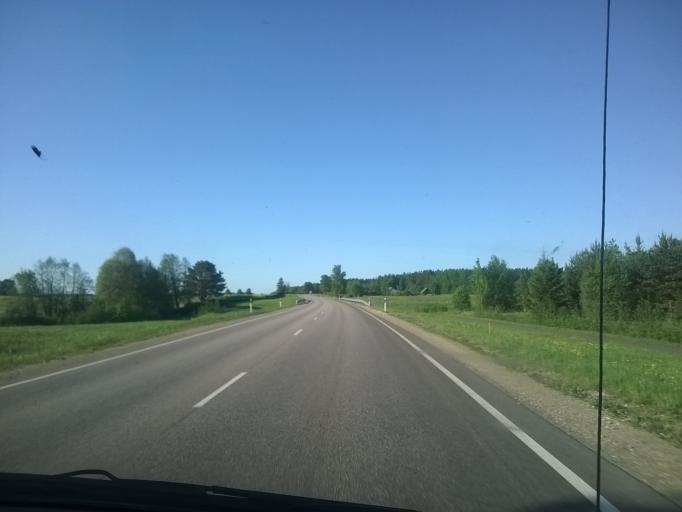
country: EE
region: Valgamaa
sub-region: Valga linn
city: Valga
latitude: 57.8440
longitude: 26.1276
